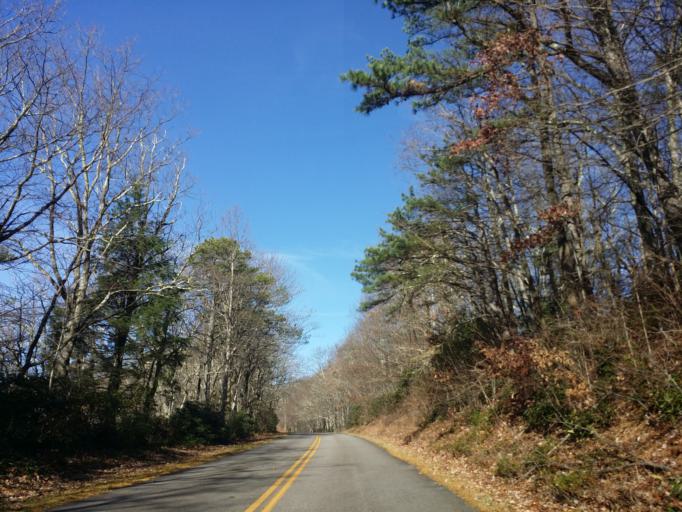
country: US
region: North Carolina
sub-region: Mitchell County
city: Spruce Pine
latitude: 35.7827
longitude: -82.1638
